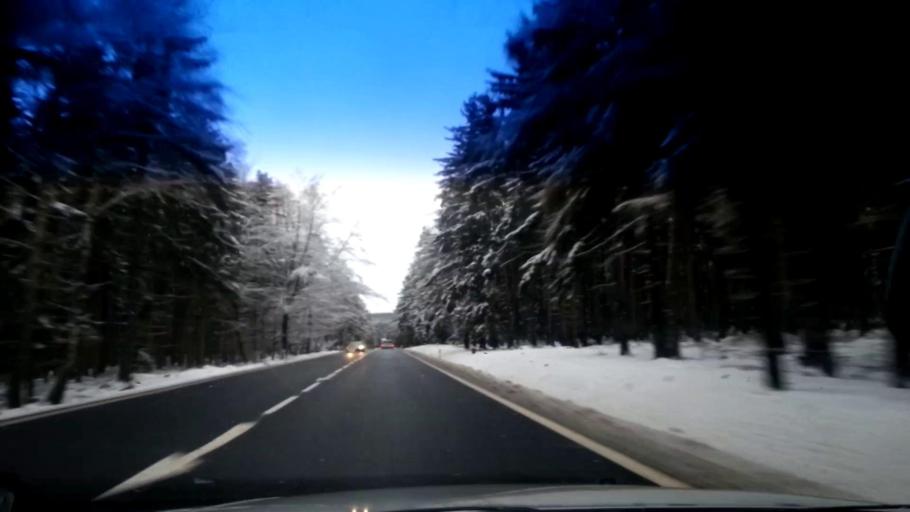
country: CZ
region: Karlovarsky
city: Hazlov
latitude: 50.1784
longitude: 12.2506
